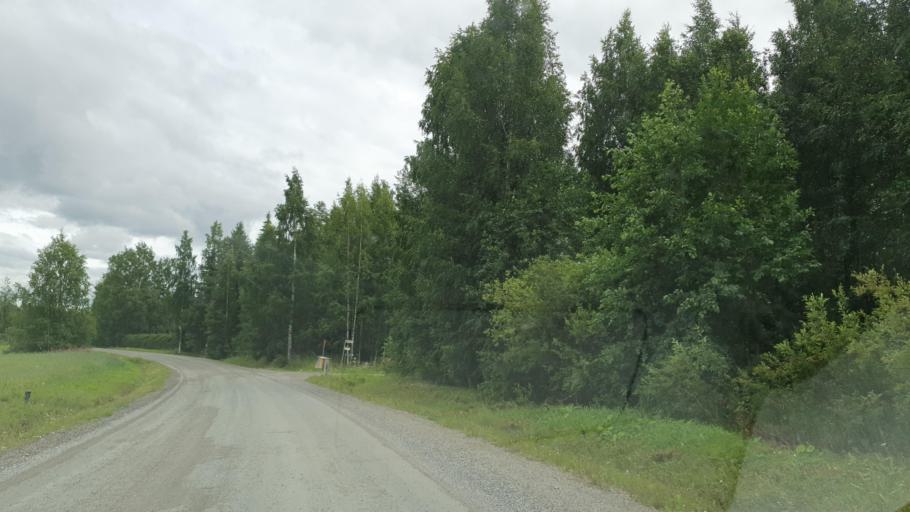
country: FI
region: Northern Savo
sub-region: Ylae-Savo
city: Iisalmi
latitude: 63.5372
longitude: 27.0770
